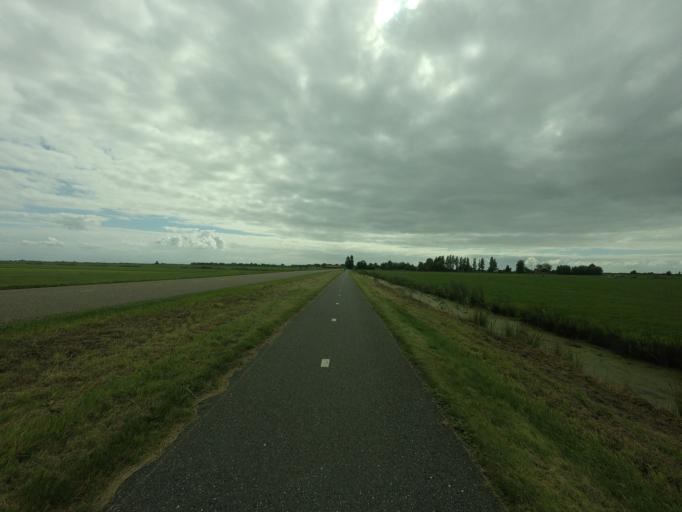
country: NL
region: Friesland
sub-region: Sudwest Fryslan
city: Heeg
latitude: 52.9798
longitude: 5.5436
